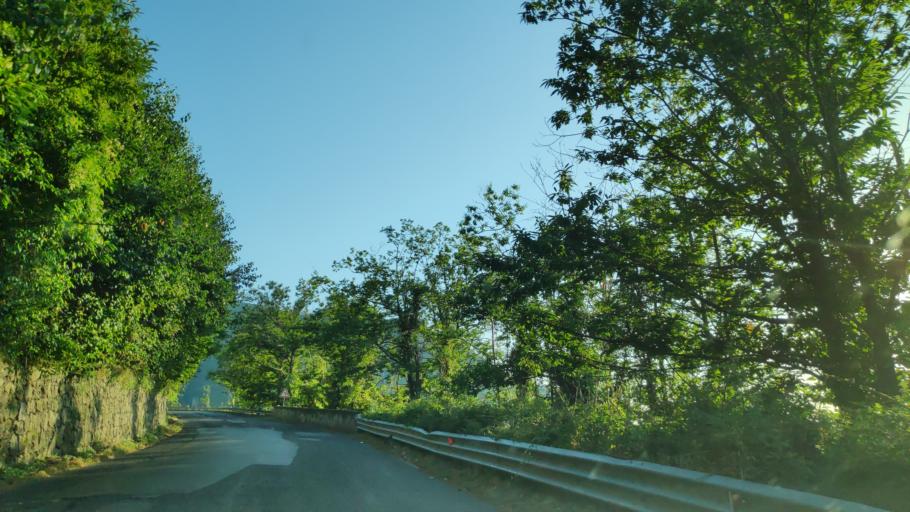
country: IT
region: Campania
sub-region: Provincia di Salerno
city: Corbara
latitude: 40.7200
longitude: 14.6039
